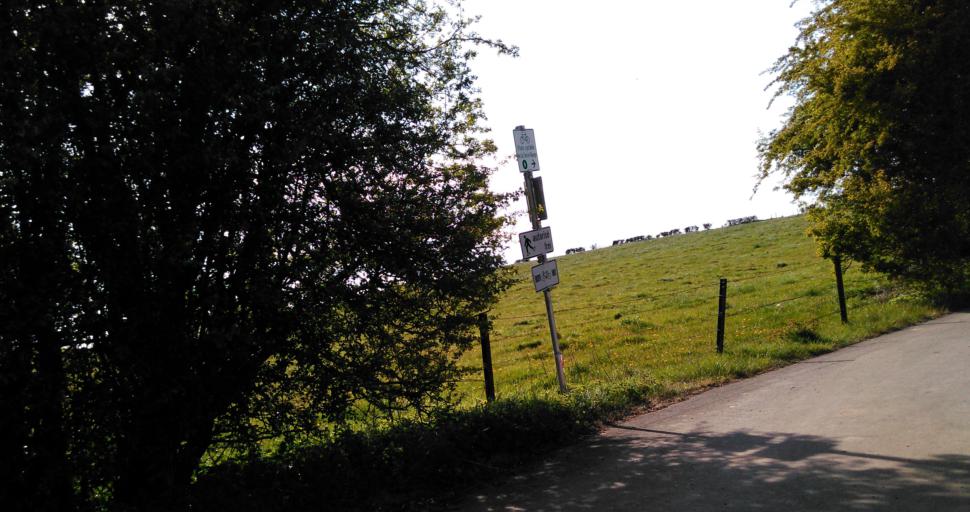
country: LU
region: Luxembourg
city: Belvaux
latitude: 49.4989
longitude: 5.9332
